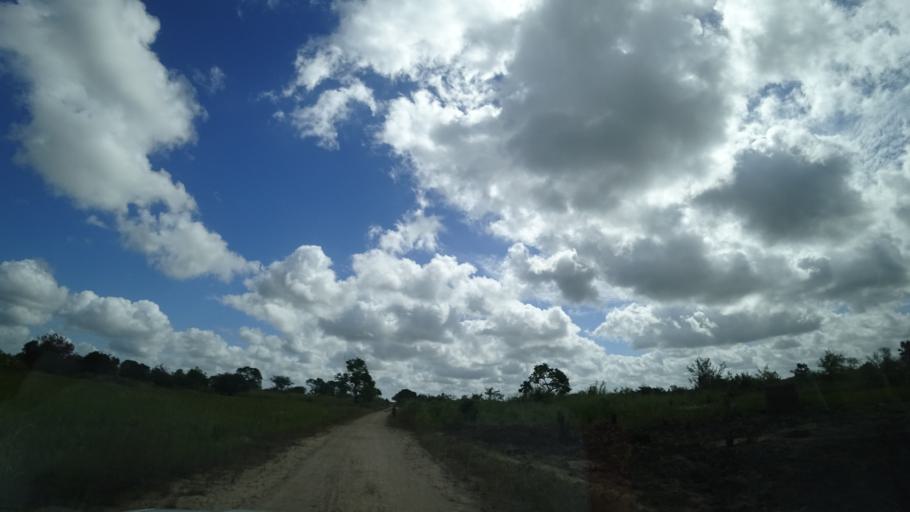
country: MZ
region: Sofala
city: Dondo
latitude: -19.3845
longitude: 34.5926
